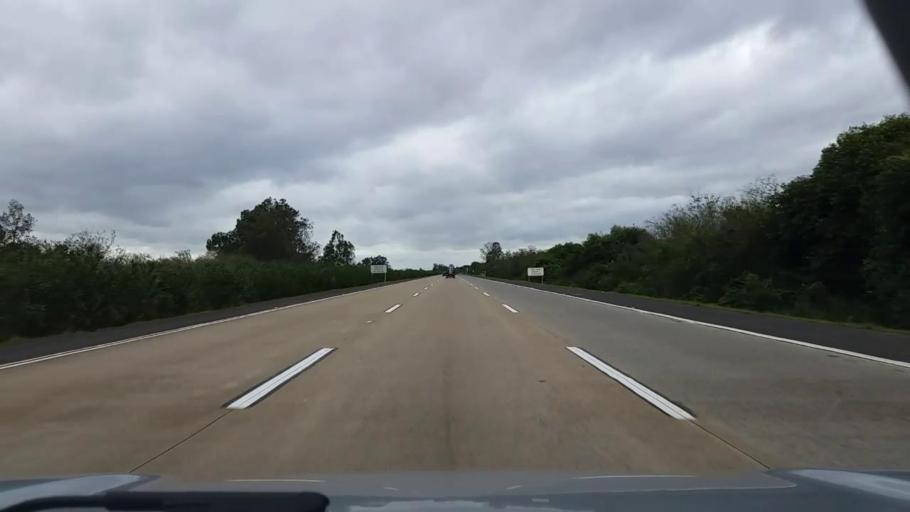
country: BR
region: Rio Grande do Sul
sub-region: Rolante
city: Rolante
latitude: -29.8852
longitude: -50.5800
